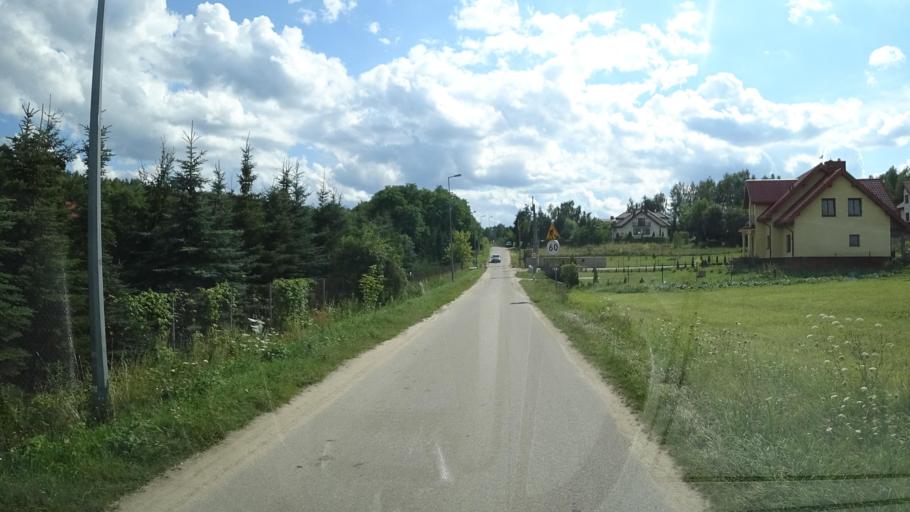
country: PL
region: Podlasie
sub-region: Powiat lomzynski
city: Piatnica
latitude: 53.1476
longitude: 22.1329
